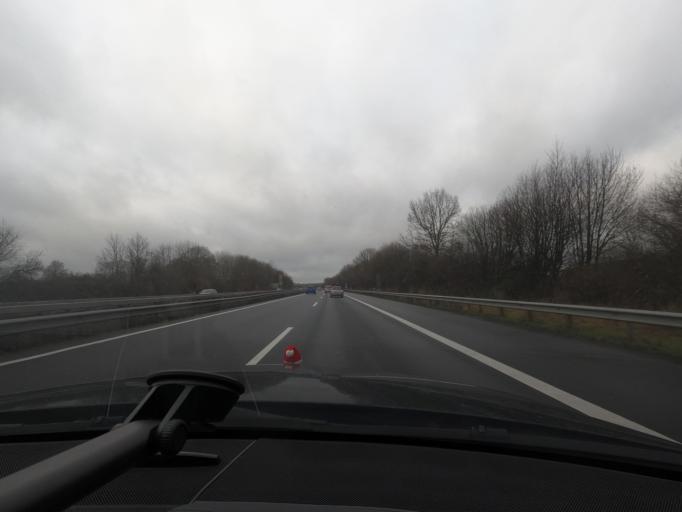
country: DE
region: Schleswig-Holstein
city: Schonbek
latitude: 54.1758
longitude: 9.9548
